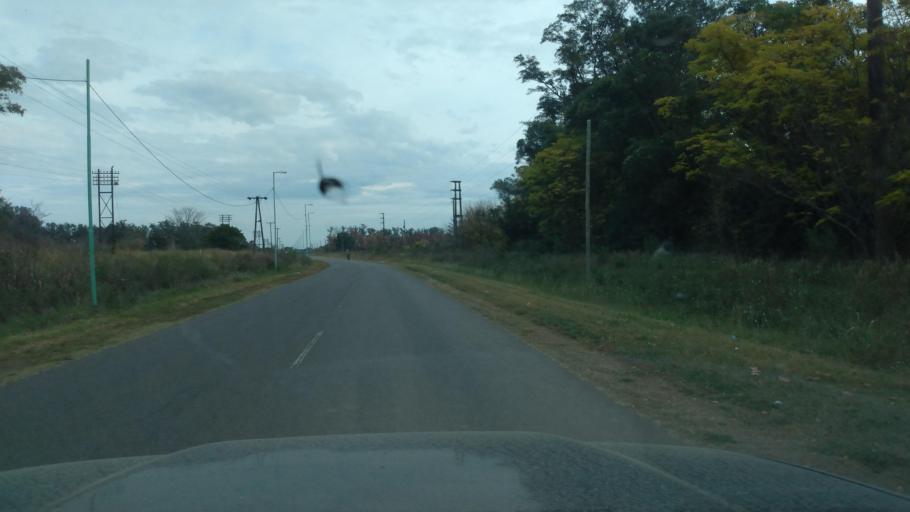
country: AR
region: Buenos Aires
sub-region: Partido de Lujan
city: Lujan
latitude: -34.5954
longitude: -59.1583
